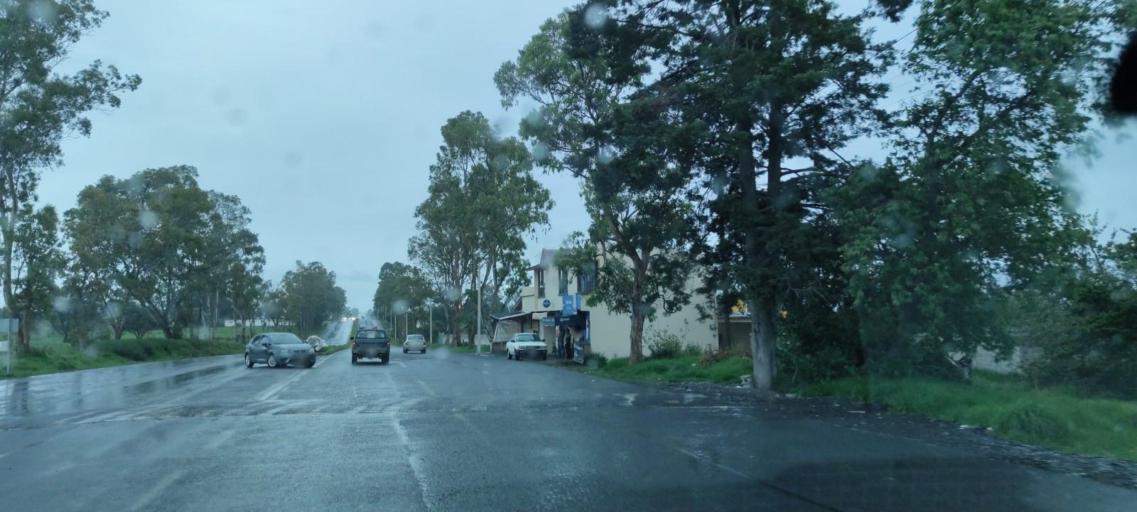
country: MX
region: Mexico
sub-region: Jilotepec
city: Doxhicho
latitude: 19.9135
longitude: -99.6041
